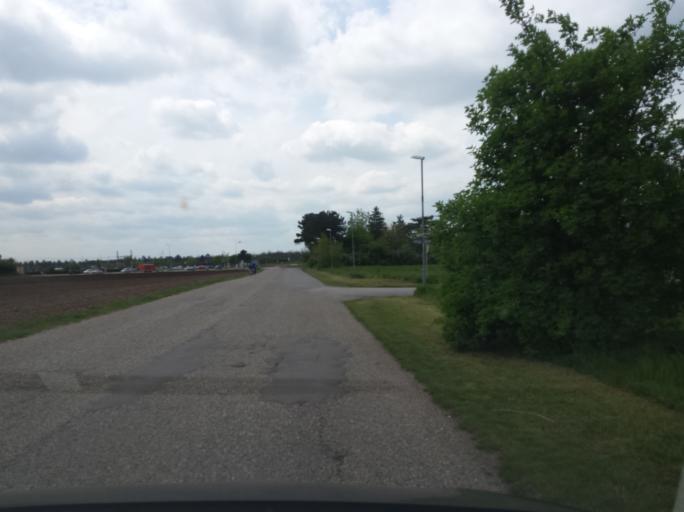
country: AT
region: Lower Austria
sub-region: Politischer Bezirk Ganserndorf
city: Parbasdorf
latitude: 48.3127
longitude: 16.5989
